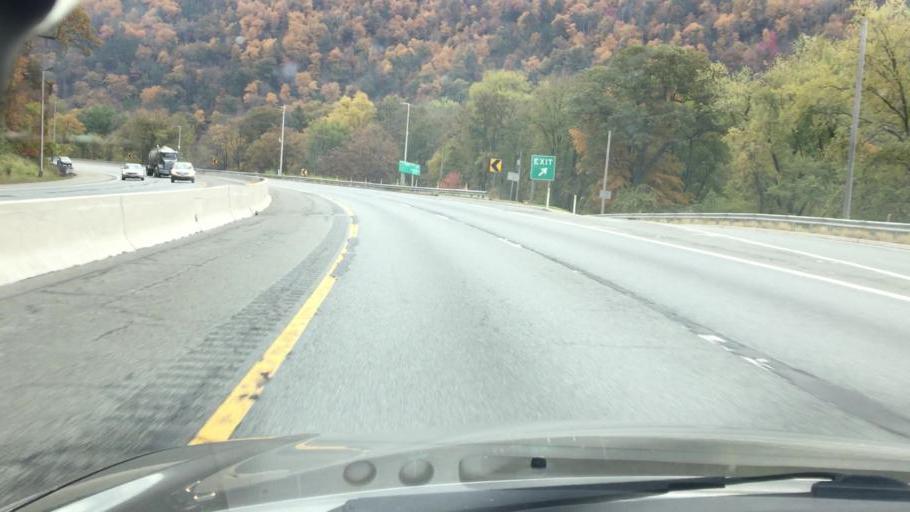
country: US
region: Pennsylvania
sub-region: Monroe County
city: East Stroudsburg
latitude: 40.9717
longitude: -75.1325
